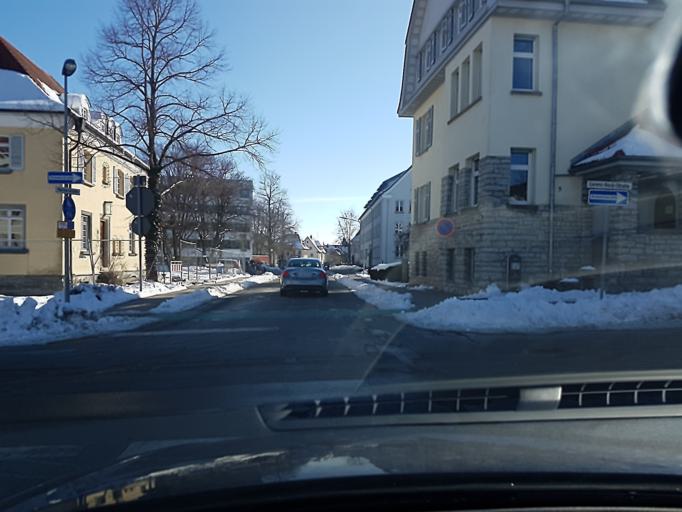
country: DE
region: Baden-Wuerttemberg
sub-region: Freiburg Region
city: Rottweil
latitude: 48.1632
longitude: 8.6280
